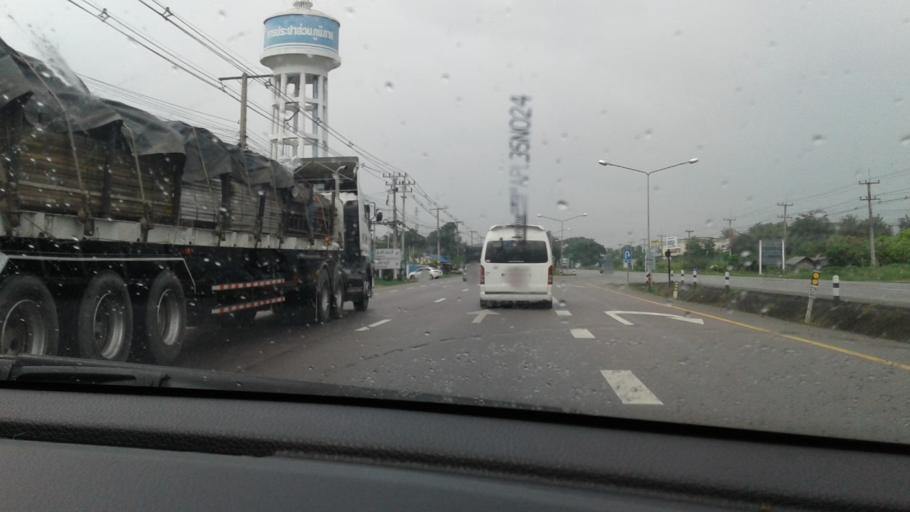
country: TH
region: Prachuap Khiri Khan
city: Kui Buri
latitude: 12.0725
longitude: 99.8587
